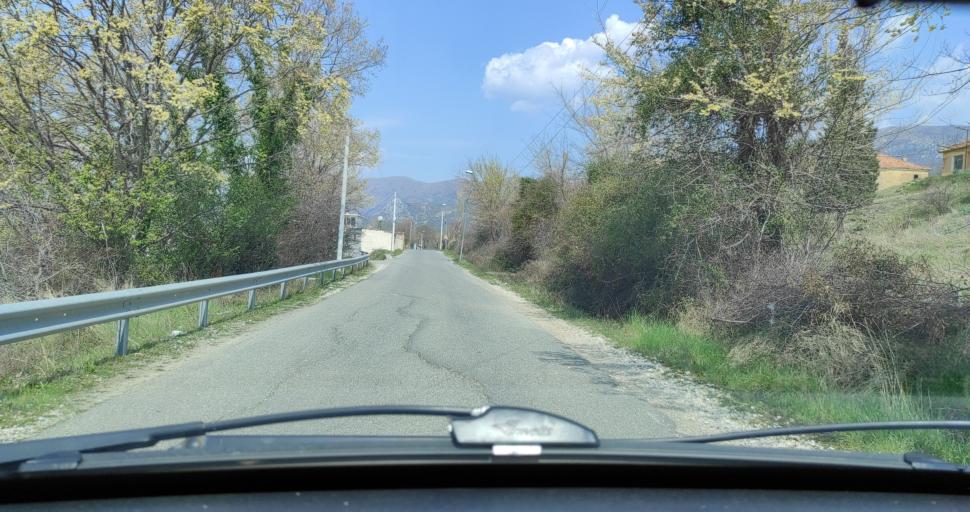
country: AL
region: Lezhe
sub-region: Rrethi i Lezhes
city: Kallmeti i Madh
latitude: 41.8543
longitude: 19.6948
